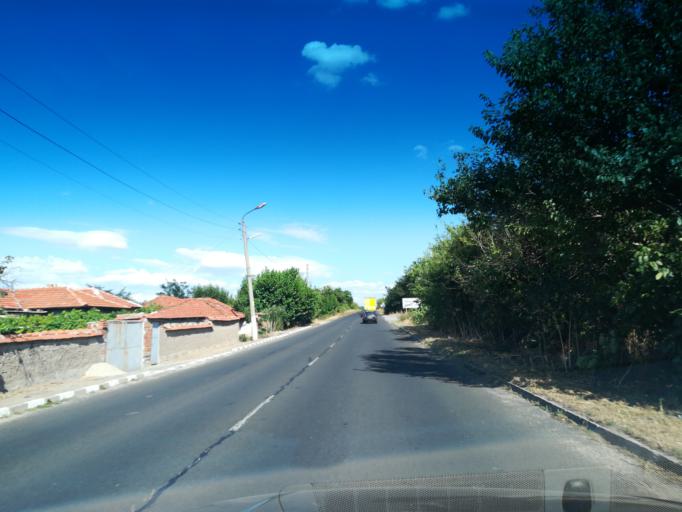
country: BG
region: Stara Zagora
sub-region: Obshtina Chirpan
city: Chirpan
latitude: 42.0589
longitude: 25.2728
